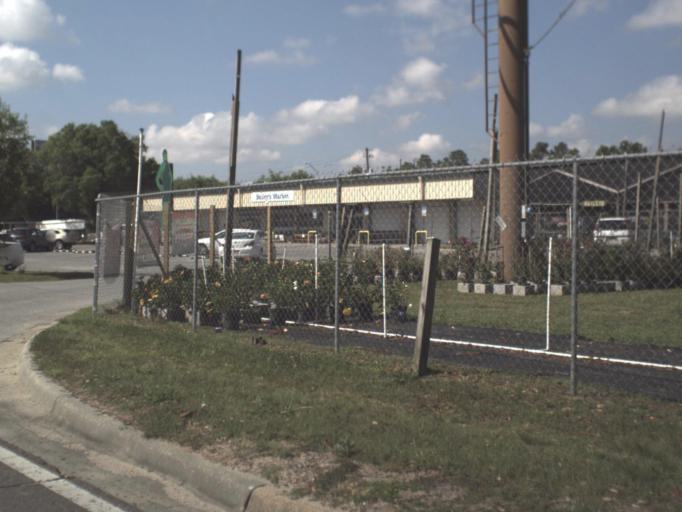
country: US
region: Florida
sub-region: Escambia County
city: Brent
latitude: 30.4606
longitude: -87.2238
